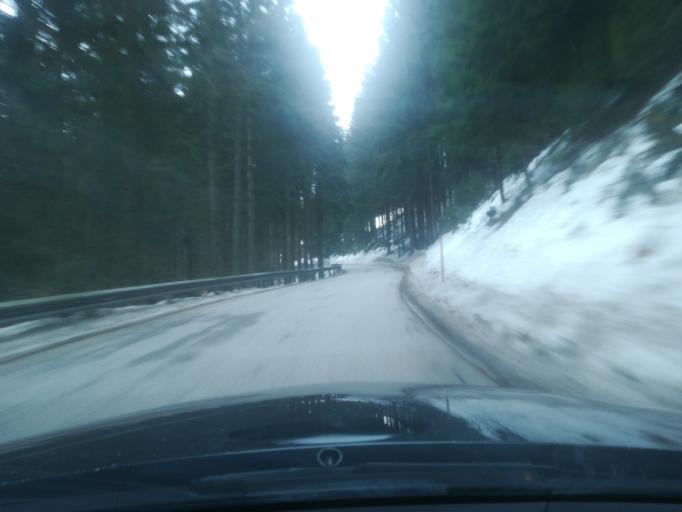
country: AT
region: Upper Austria
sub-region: Politischer Bezirk Perg
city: Perg
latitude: 48.3737
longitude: 14.6302
